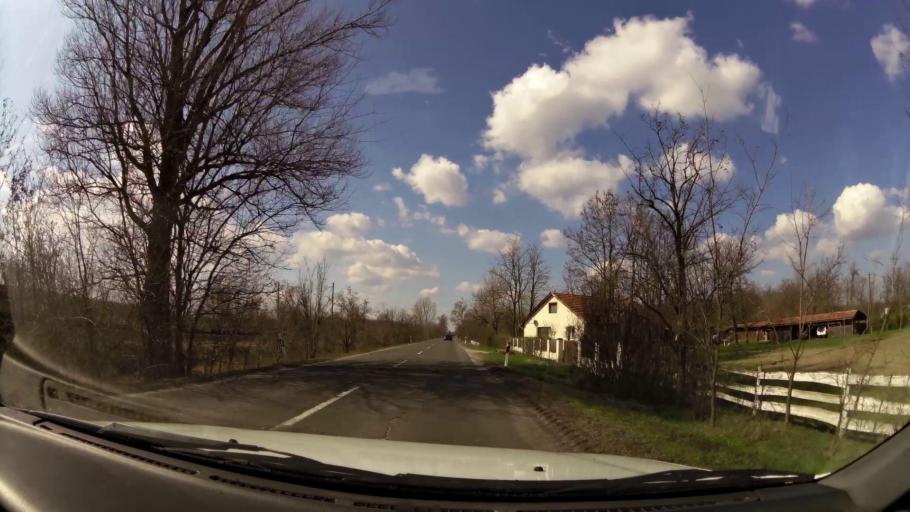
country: HU
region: Pest
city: Nagykata
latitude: 47.3920
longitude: 19.7683
